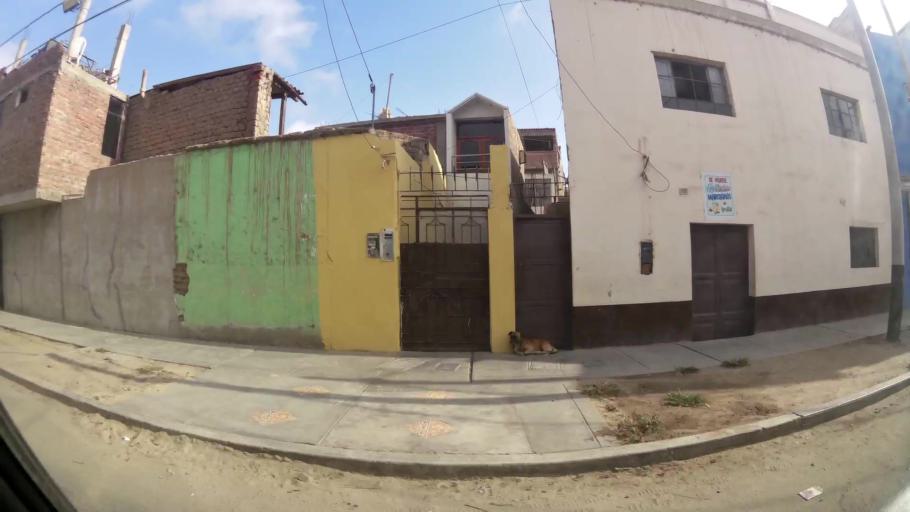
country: PE
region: La Libertad
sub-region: Provincia de Trujillo
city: Trujillo
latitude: -8.1042
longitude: -79.0166
